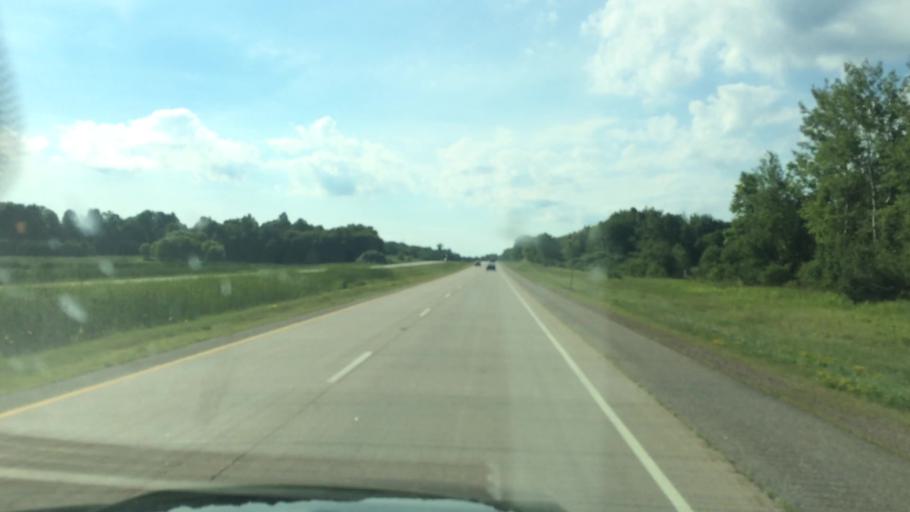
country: US
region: Wisconsin
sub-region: Shawano County
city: Wittenberg
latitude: 44.8141
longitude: -89.0466
